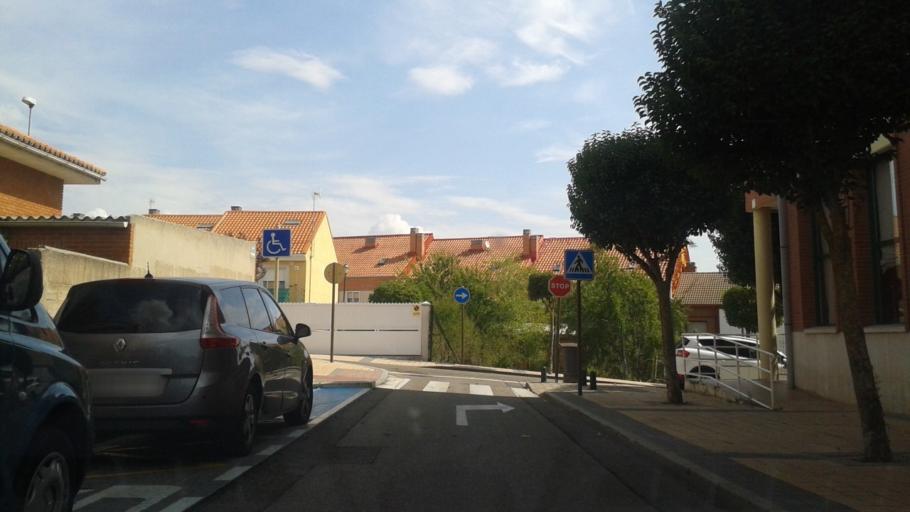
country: ES
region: Castille and Leon
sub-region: Provincia de Valladolid
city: Arroyo
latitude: 41.6263
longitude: -4.7736
